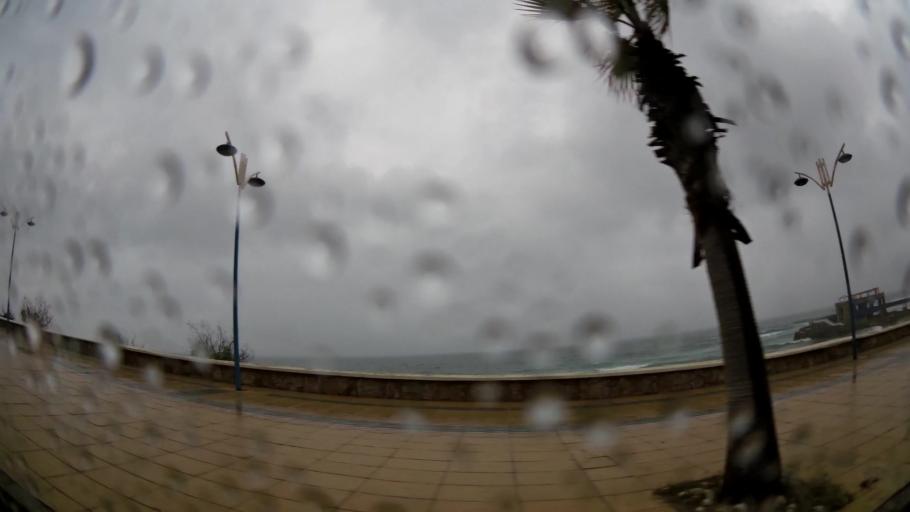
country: MA
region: Taza-Al Hoceima-Taounate
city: Tirhanimine
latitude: 35.2466
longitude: -3.9591
